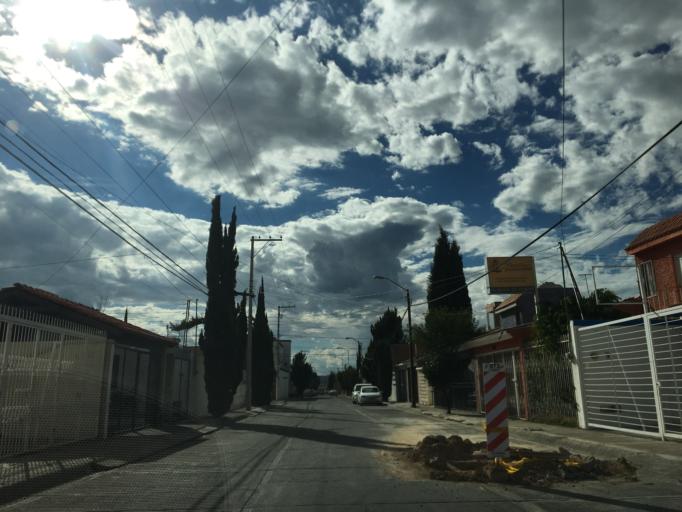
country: MX
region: Aguascalientes
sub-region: Jesus Maria
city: El Llano
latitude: 21.9286
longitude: -102.3025
